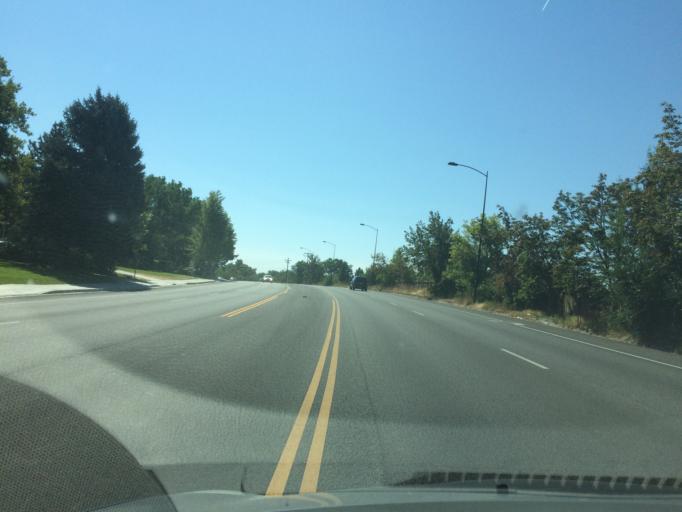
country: US
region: Utah
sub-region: Weber County
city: Washington Terrace
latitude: 41.1745
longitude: -111.9493
